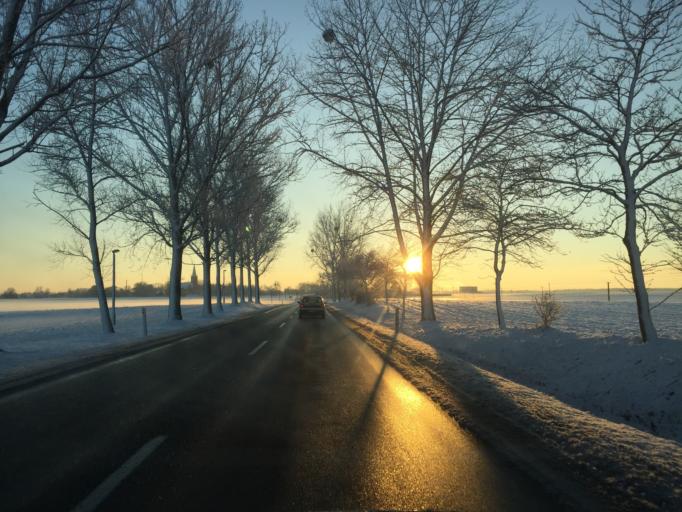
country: PL
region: Kujawsko-Pomorskie
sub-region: Powiat golubsko-dobrzynski
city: Kowalewo Pomorskie
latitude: 53.1247
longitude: 18.8379
